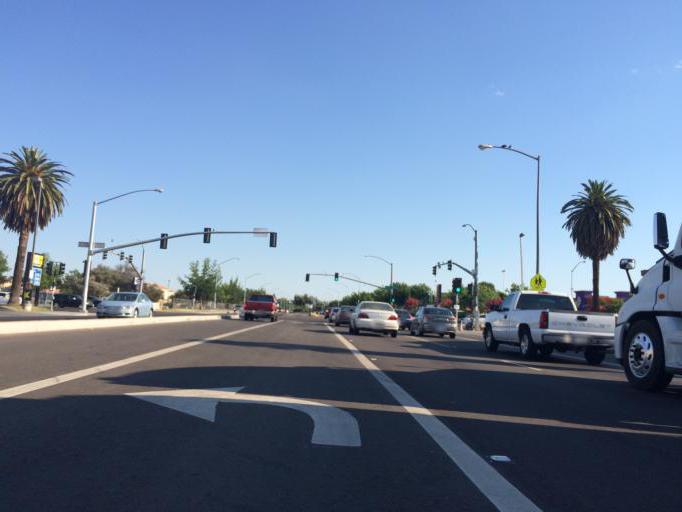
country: US
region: California
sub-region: Fresno County
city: Sunnyside
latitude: 36.7365
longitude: -119.7184
